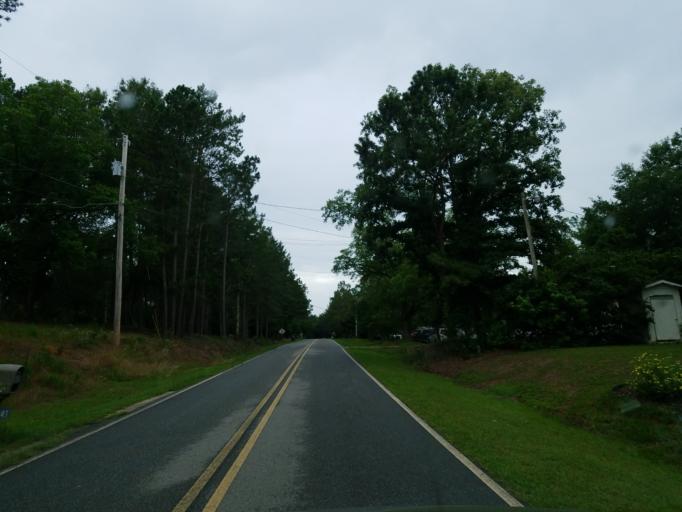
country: US
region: Georgia
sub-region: Crisp County
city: Cordele
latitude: 31.9755
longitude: -83.6986
